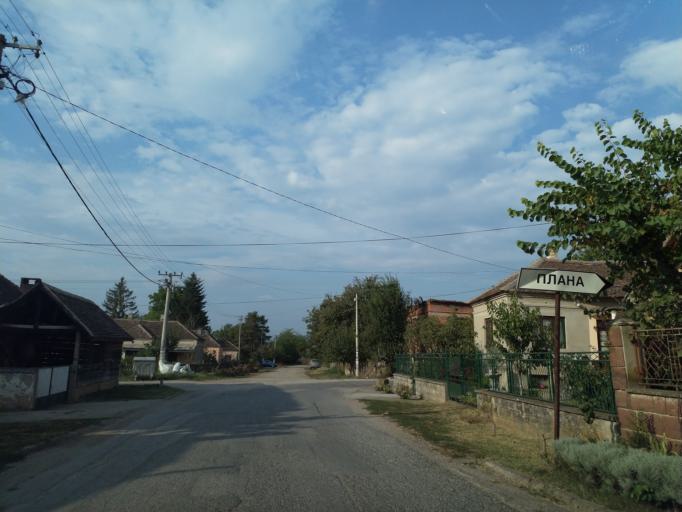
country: RS
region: Central Serbia
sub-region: Pomoravski Okrug
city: Paracin
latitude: 43.8441
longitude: 21.4804
